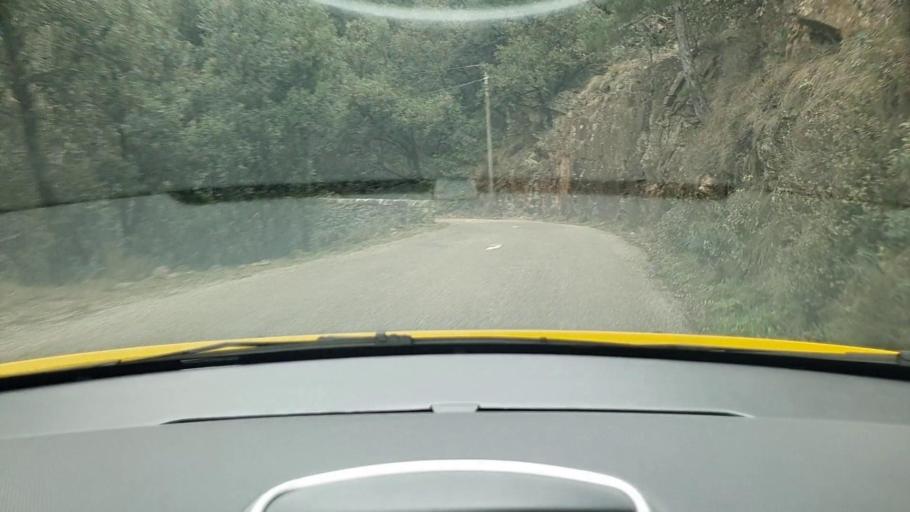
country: FR
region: Languedoc-Roussillon
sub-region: Departement du Gard
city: Besseges
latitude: 44.3696
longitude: 4.0431
